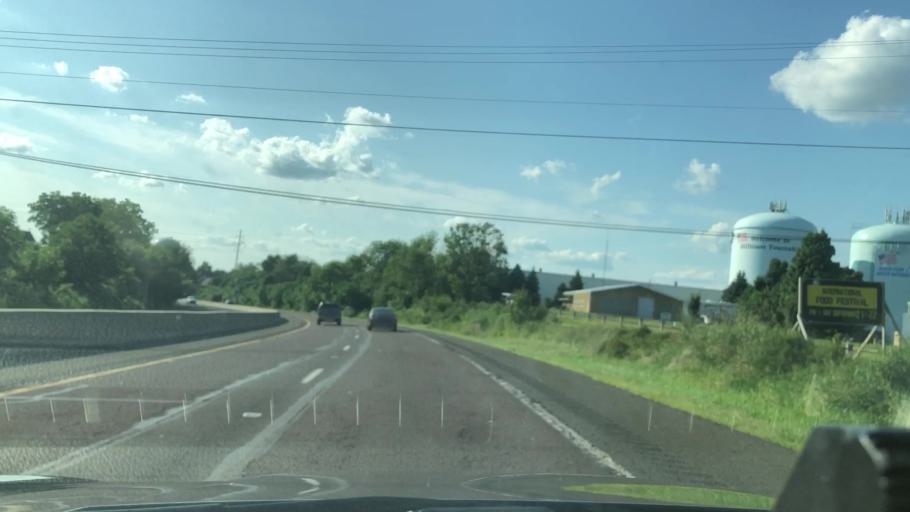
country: US
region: Pennsylvania
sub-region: Montgomery County
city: Souderton
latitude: 40.3130
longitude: -75.3004
